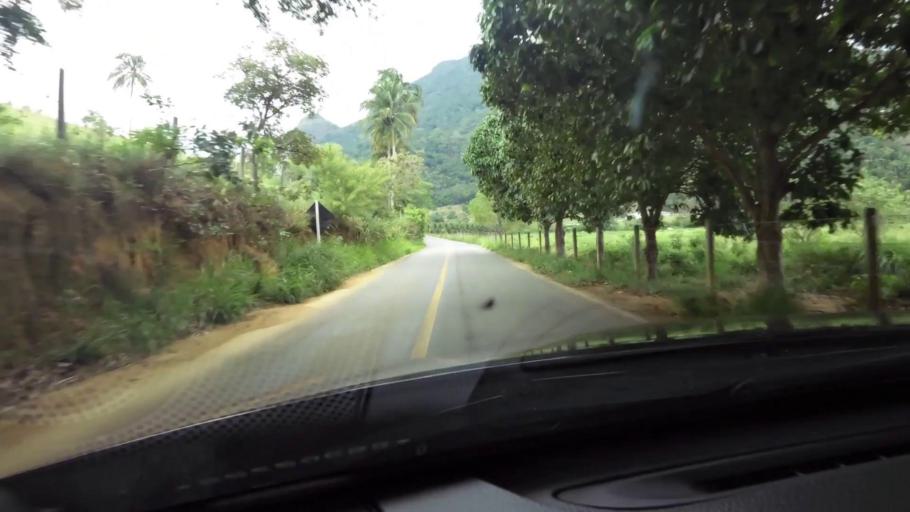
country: BR
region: Espirito Santo
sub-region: Guarapari
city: Guarapari
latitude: -20.6205
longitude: -40.5286
